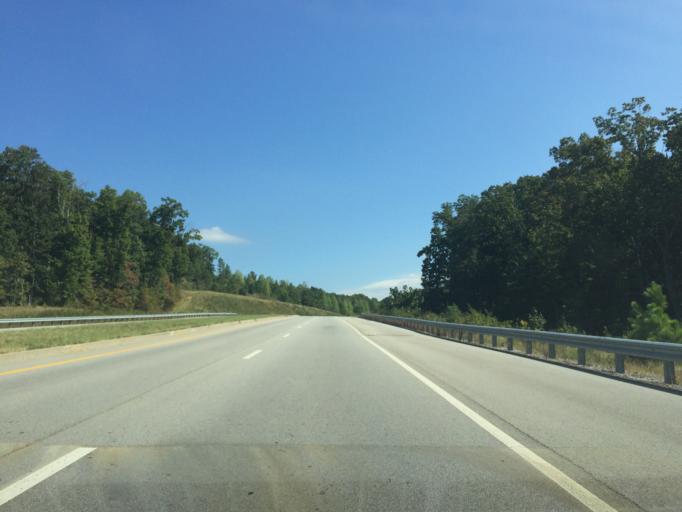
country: US
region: Tennessee
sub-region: Hamilton County
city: Harrison
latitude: 35.0741
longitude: -85.1196
